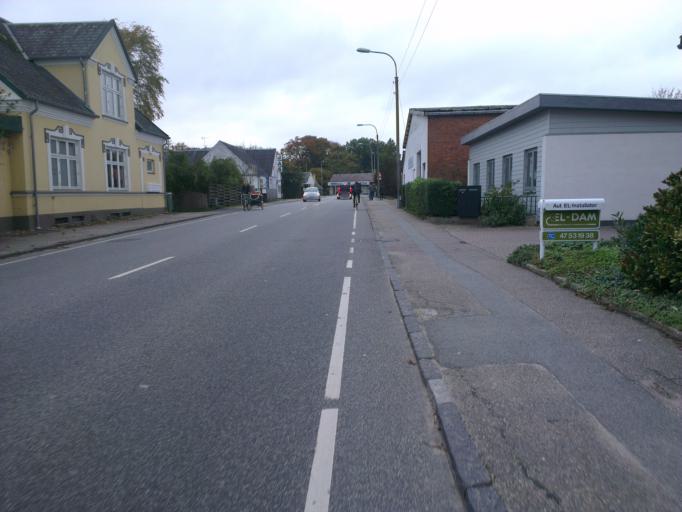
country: DK
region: Capital Region
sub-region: Frederikssund Kommune
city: Jaegerspris
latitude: 55.8541
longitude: 11.9842
